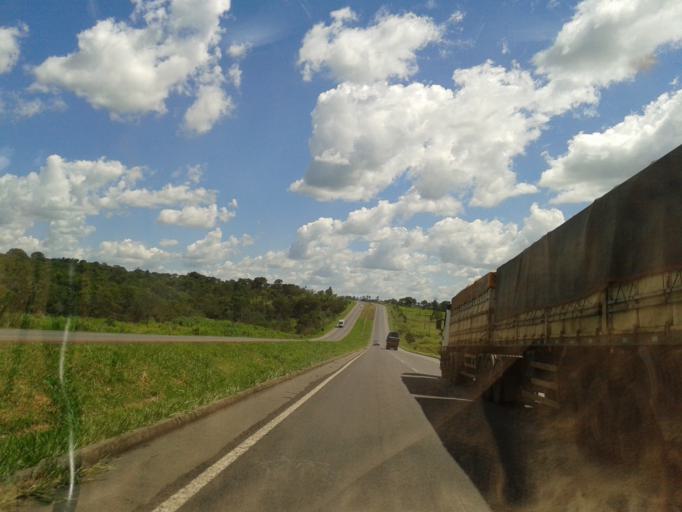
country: BR
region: Goias
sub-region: Piracanjuba
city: Piracanjuba
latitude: -17.3535
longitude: -49.2483
